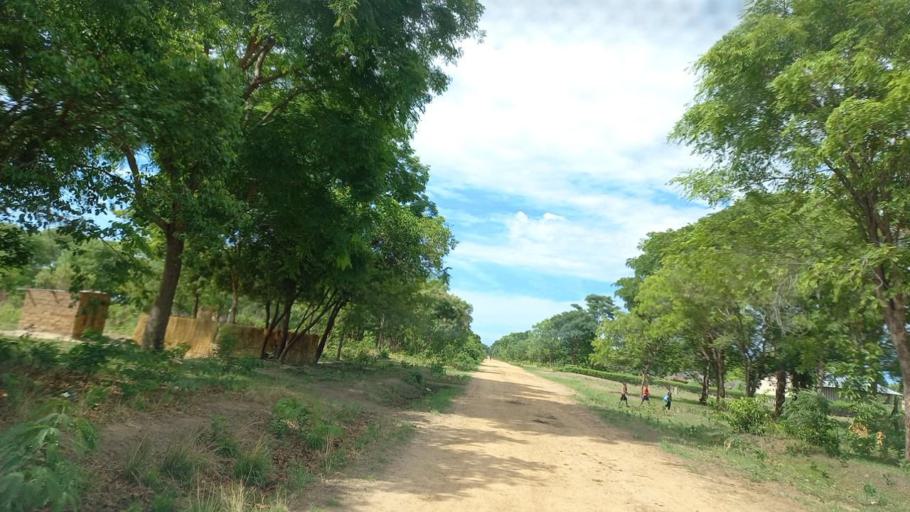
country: ZM
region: North-Western
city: Kabompo
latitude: -13.5224
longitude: 24.3833
